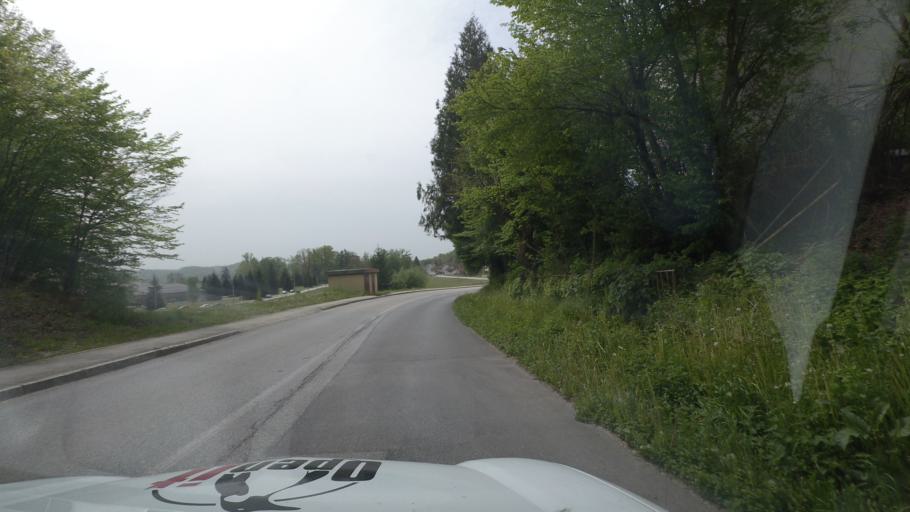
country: HR
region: Sisacko-Moslavacka
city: Gvozd
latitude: 45.2961
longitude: 15.9676
